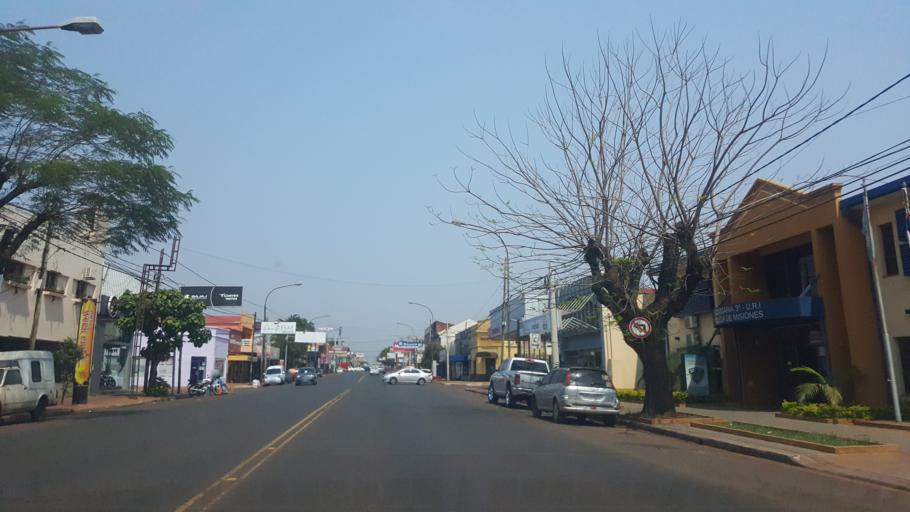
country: AR
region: Misiones
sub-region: Departamento de Capital
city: Posadas
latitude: -27.3820
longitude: -55.8996
